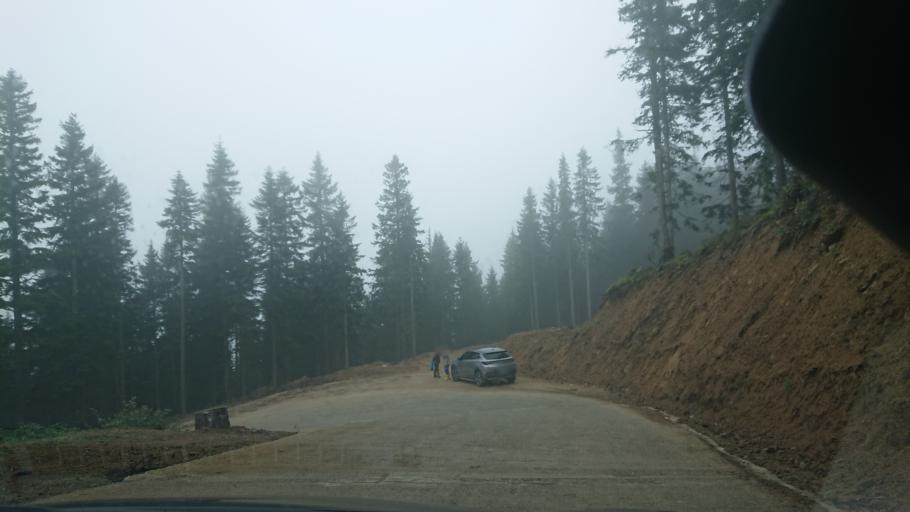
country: TR
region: Gumushane
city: Kurtun
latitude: 40.6705
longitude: 39.0094
